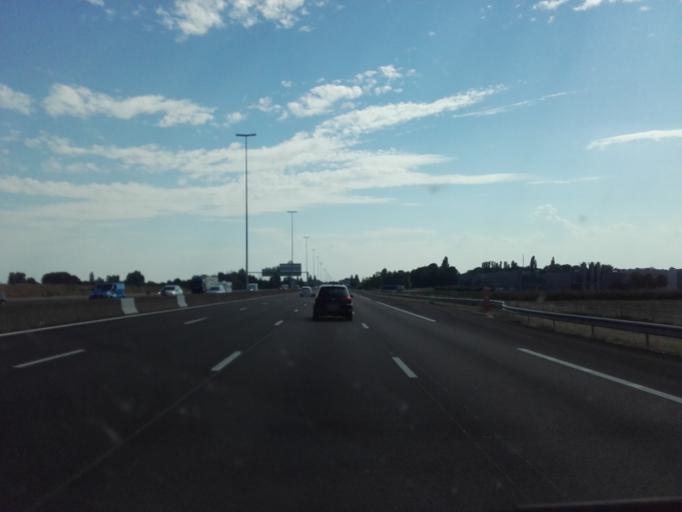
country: FR
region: Bourgogne
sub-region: Departement de la Cote-d'Or
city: Beaune
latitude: 47.0096
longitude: 4.8644
